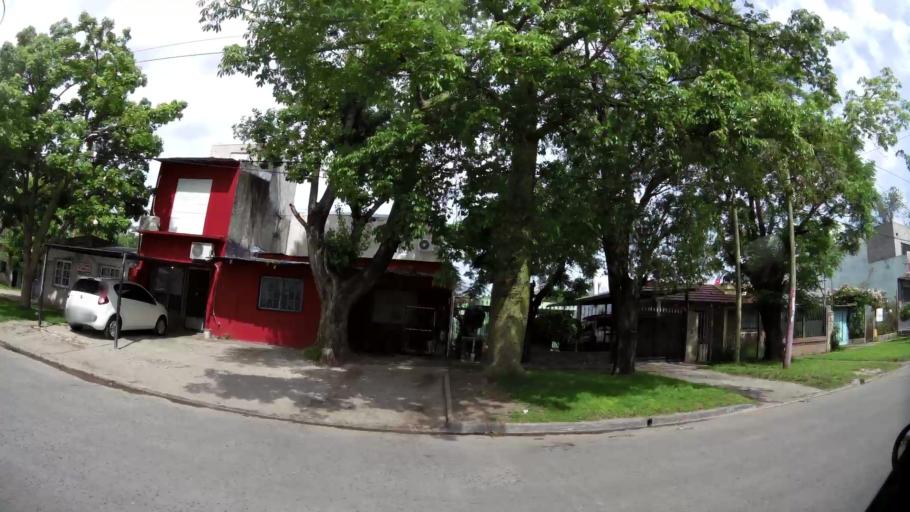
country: AR
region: Buenos Aires
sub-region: Partido de Quilmes
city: Quilmes
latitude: -34.7521
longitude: -58.2472
